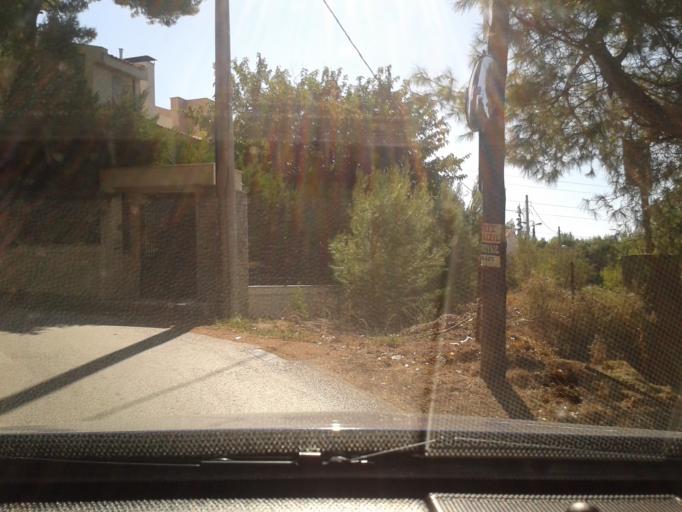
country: GR
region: Attica
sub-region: Nomarchia Anatolikis Attikis
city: Varybobi
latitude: 38.1294
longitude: 23.7873
